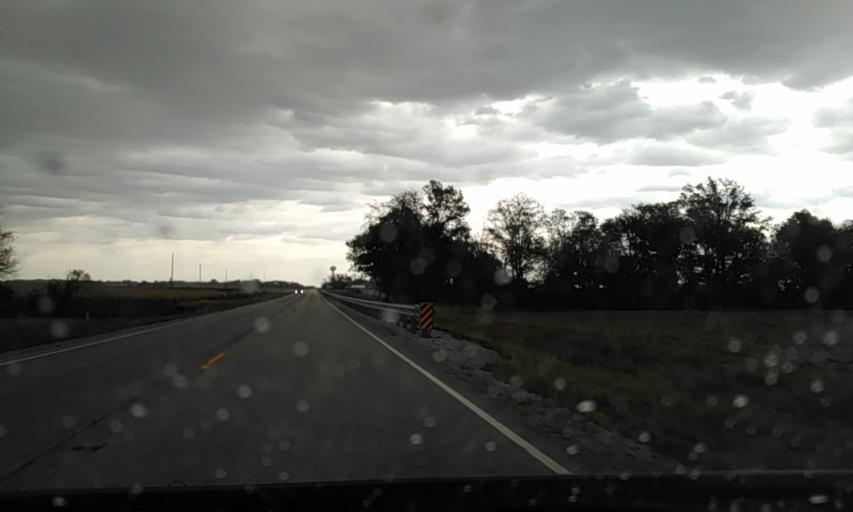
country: US
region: Illinois
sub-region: Bond County
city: Greenville
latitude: 38.8645
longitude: -89.4267
